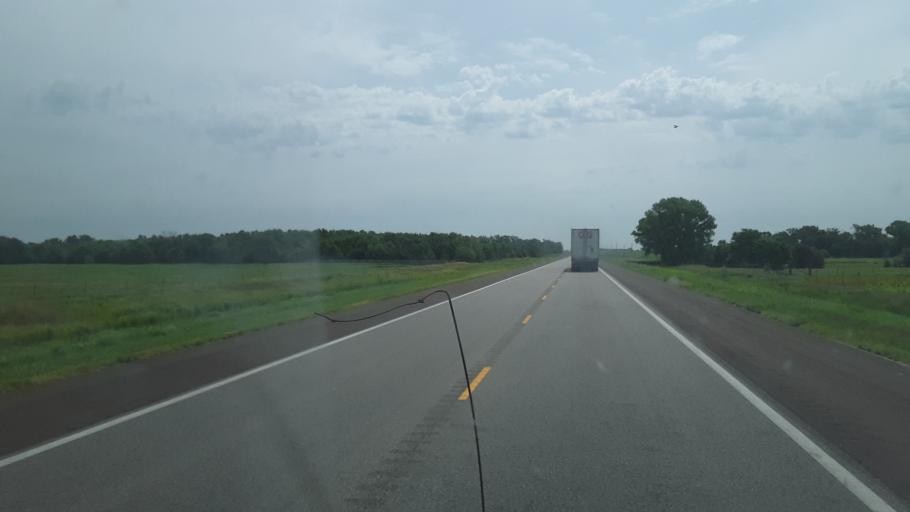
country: US
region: Kansas
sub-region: Reno County
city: Nickerson
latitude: 37.9849
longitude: -98.1453
